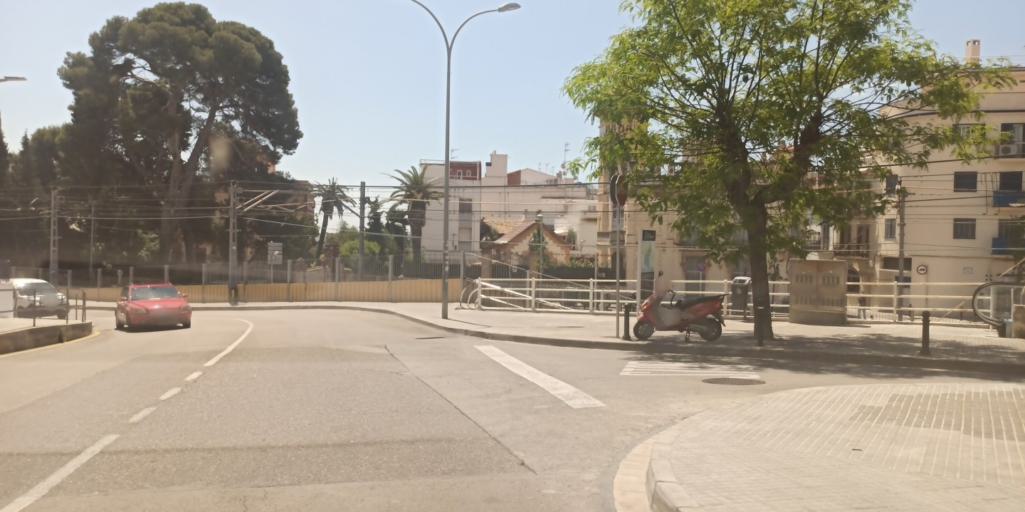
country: ES
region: Catalonia
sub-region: Provincia de Barcelona
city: Sitges
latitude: 41.2392
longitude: 1.8114
